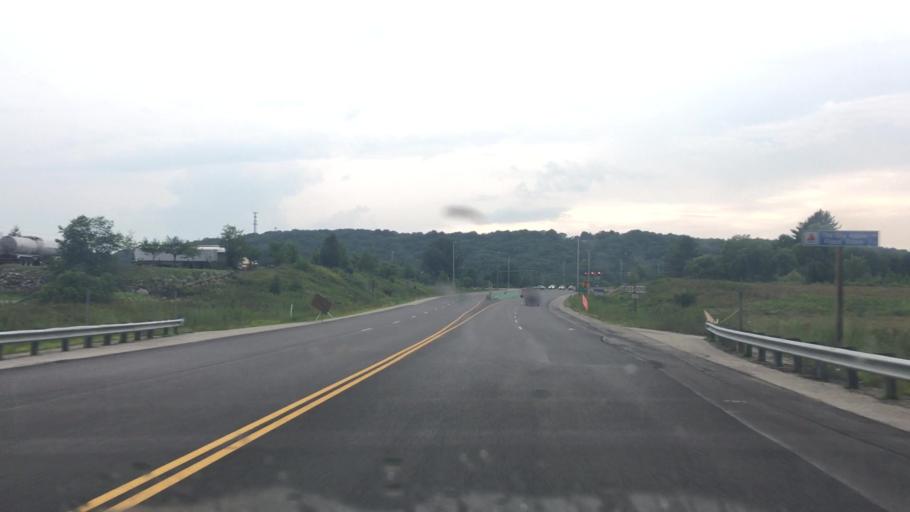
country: US
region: Maine
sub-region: Kennebec County
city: Augusta
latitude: 44.3300
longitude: -69.7567
